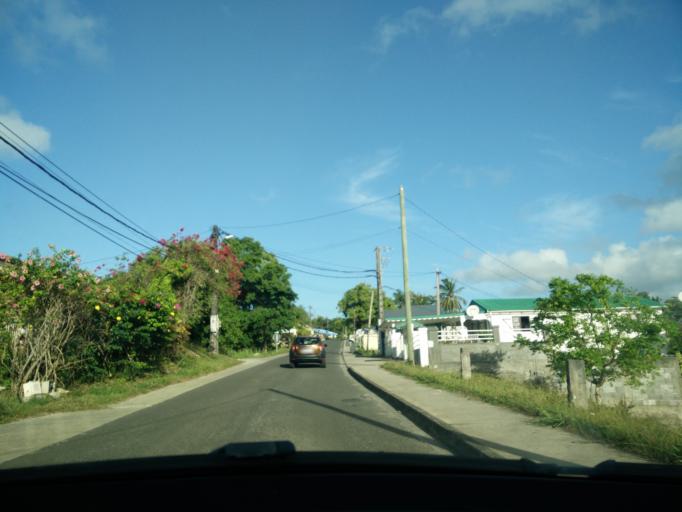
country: GP
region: Guadeloupe
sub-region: Guadeloupe
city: Sainte-Anne
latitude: 16.2786
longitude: -61.4096
